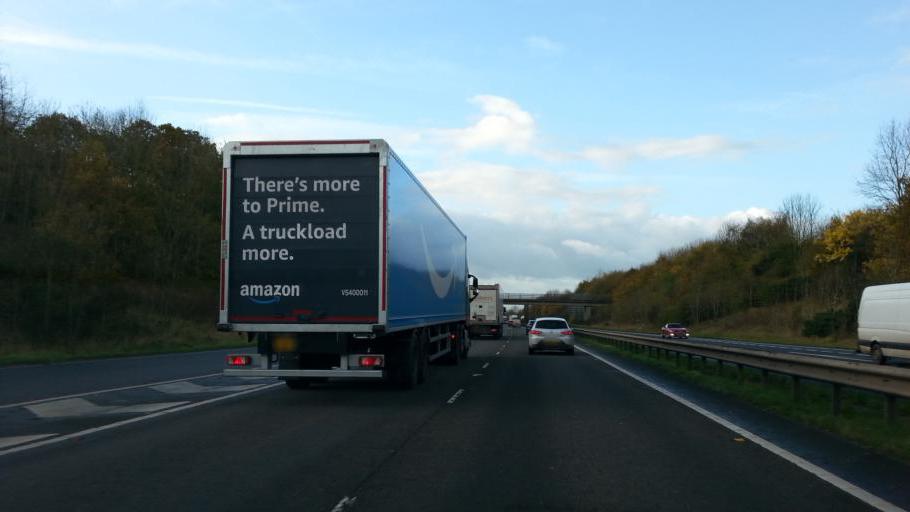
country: GB
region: England
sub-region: Leicestershire
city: Measham
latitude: 52.7238
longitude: -1.4925
